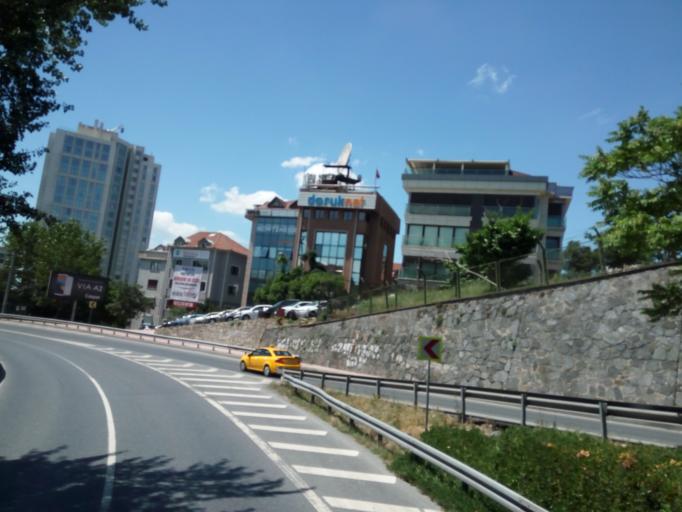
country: TR
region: Istanbul
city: Sisli
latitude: 41.0537
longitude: 29.0088
